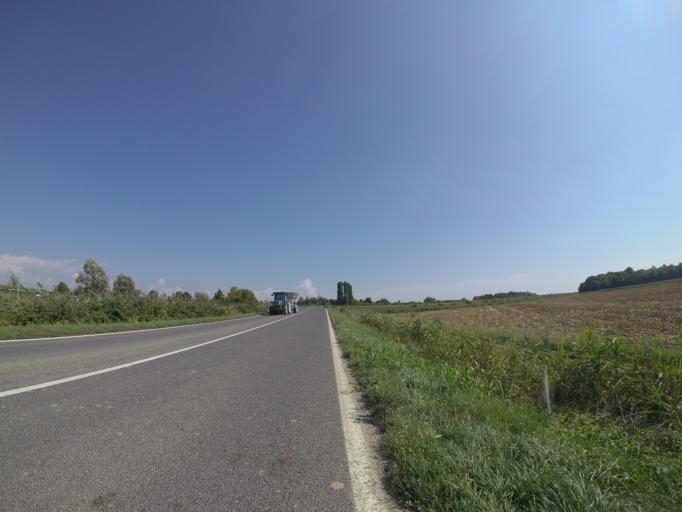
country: IT
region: Friuli Venezia Giulia
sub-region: Provincia di Udine
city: Muzzana del Turgnano
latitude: 45.8130
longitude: 13.1564
